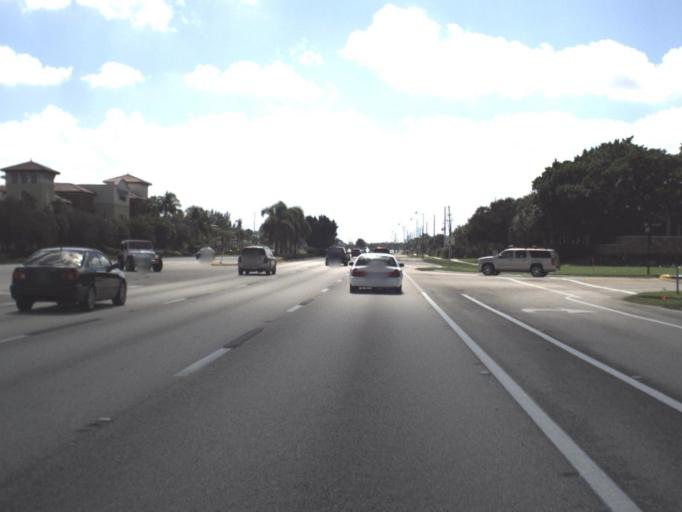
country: US
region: Florida
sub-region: Lee County
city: Estero
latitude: 26.3930
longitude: -81.8104
